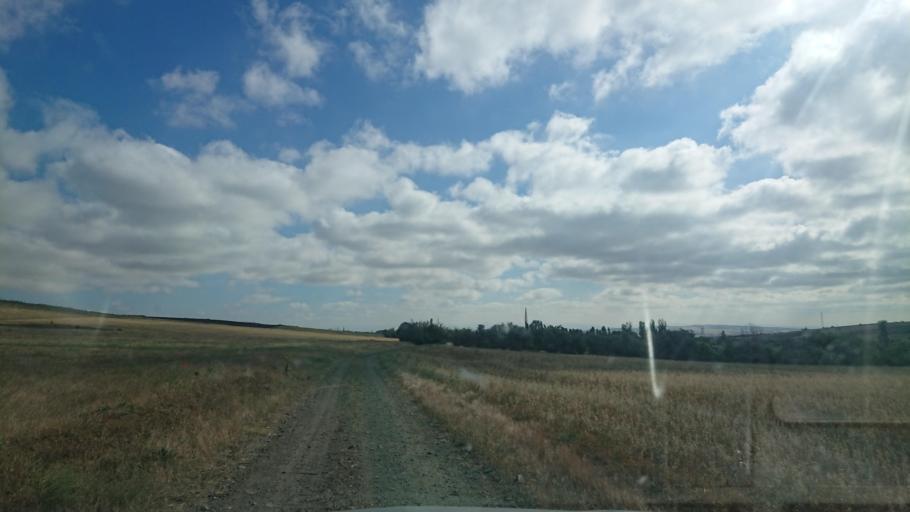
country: TR
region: Aksaray
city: Agacoren
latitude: 38.8537
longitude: 33.9316
